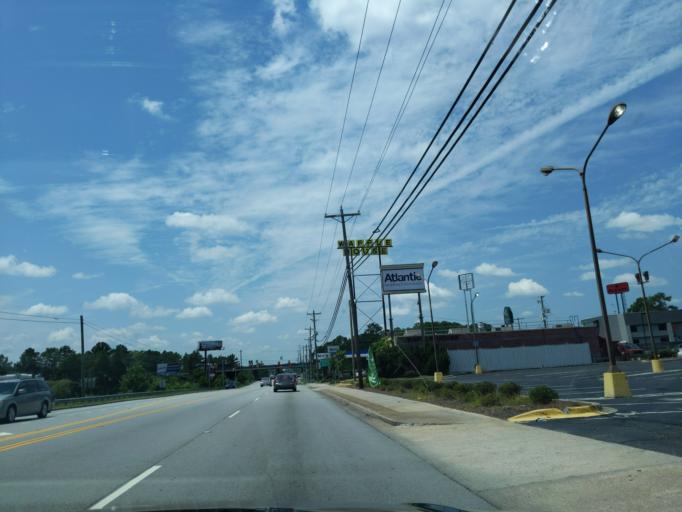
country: US
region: South Carolina
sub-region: Richland County
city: Dentsville
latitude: 34.0761
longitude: -80.9450
